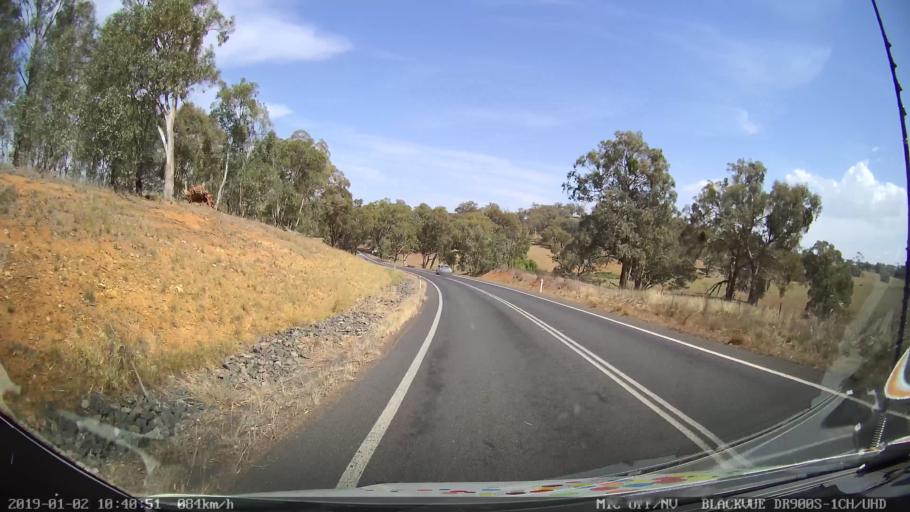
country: AU
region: New South Wales
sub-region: Cootamundra
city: Cootamundra
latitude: -34.7979
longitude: 148.3126
